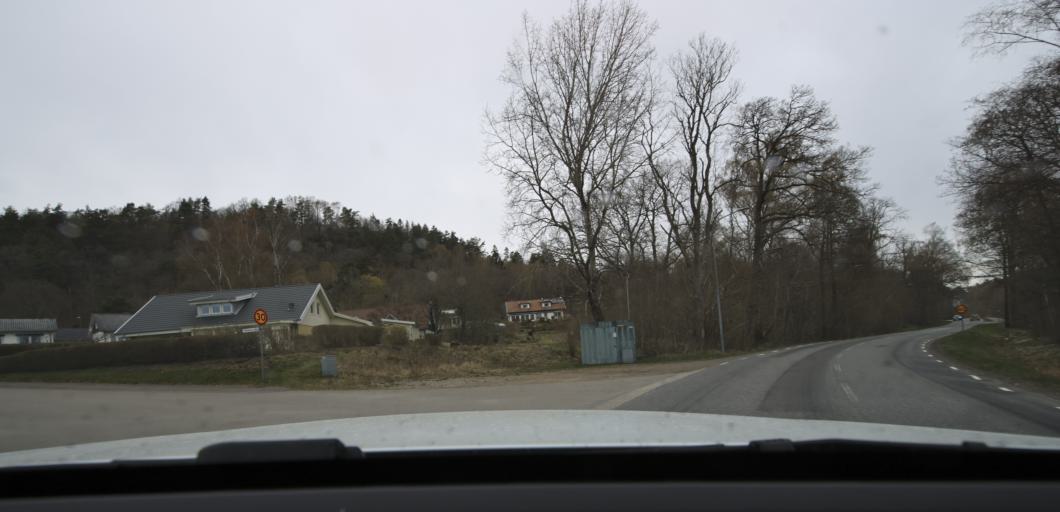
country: SE
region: Halland
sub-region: Varbergs Kommun
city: Tvaaker
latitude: 57.1479
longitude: 12.4609
